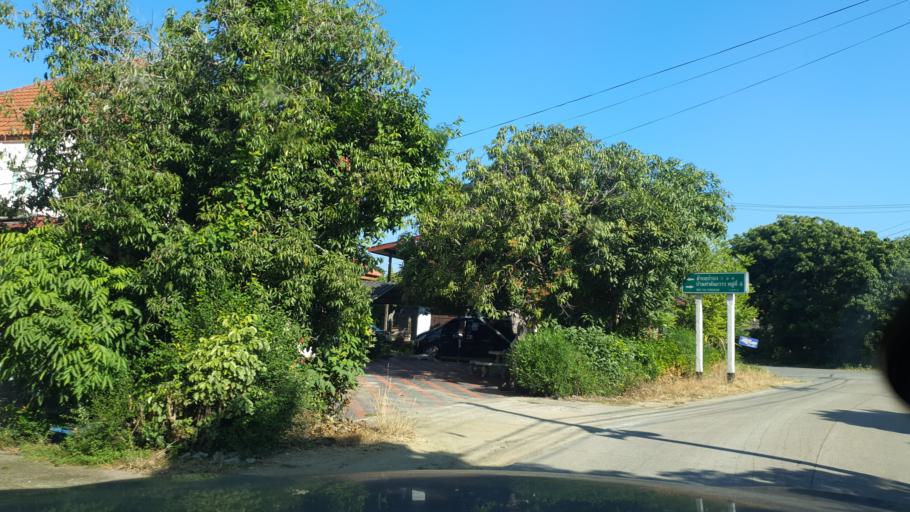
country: TH
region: Chiang Mai
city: Saraphi
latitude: 18.7272
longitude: 99.0625
